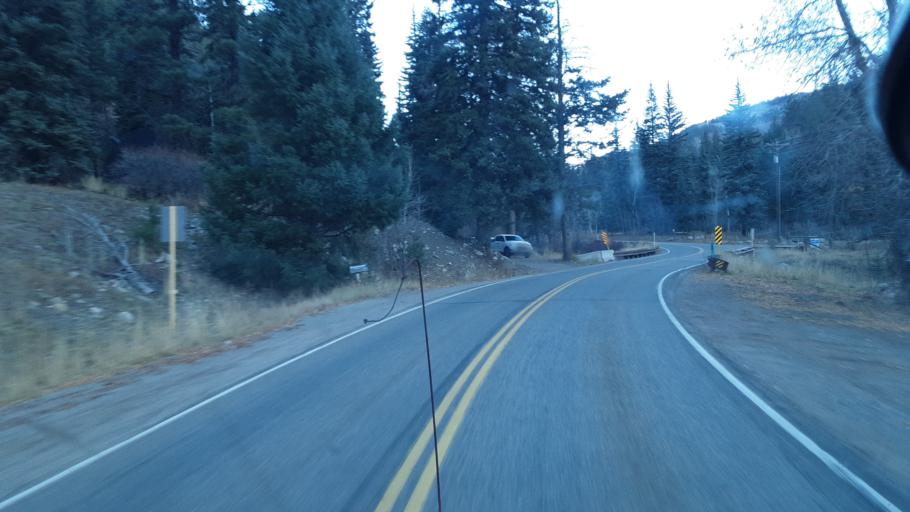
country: US
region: Colorado
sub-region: La Plata County
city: Bayfield
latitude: 37.3672
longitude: -107.6669
